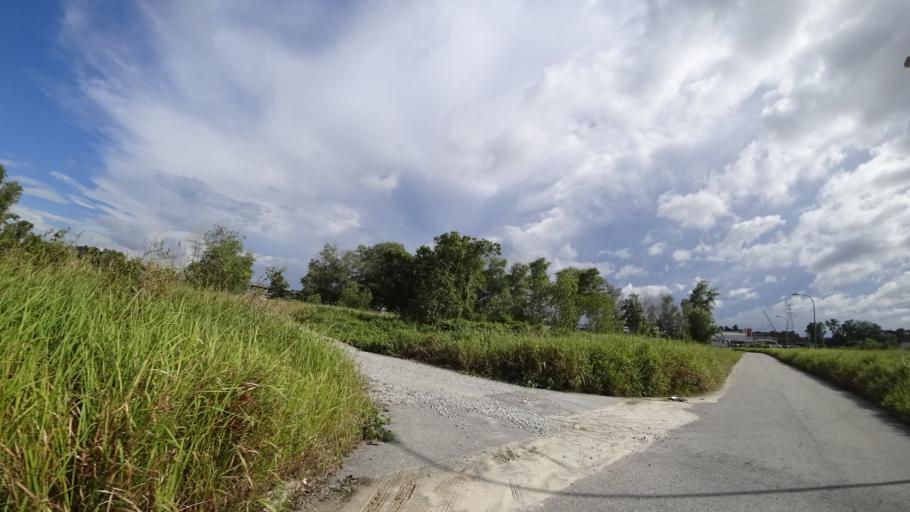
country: BN
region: Brunei and Muara
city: Bandar Seri Begawan
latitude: 4.8967
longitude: 114.9039
